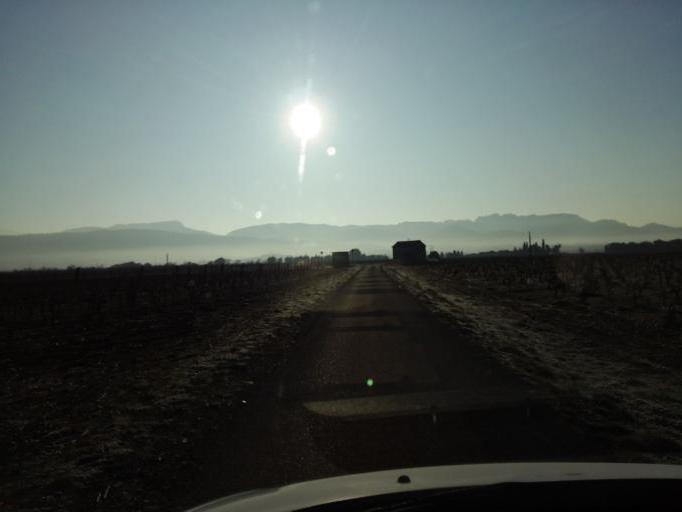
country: FR
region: Provence-Alpes-Cote d'Azur
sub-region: Departement du Vaucluse
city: Sablet
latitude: 44.2058
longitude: 4.9780
